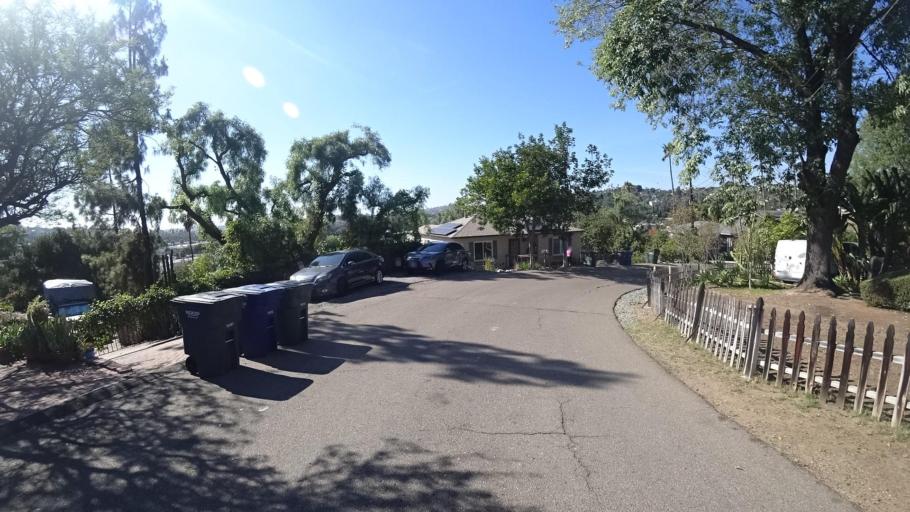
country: US
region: California
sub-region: San Diego County
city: Spring Valley
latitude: 32.7499
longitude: -116.9824
